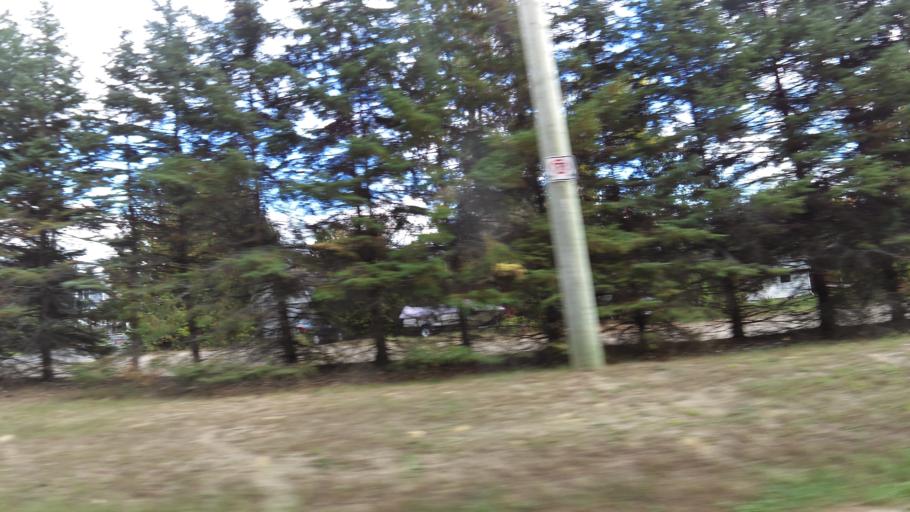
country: CA
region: Ontario
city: Deep River
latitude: 46.0947
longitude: -77.4833
